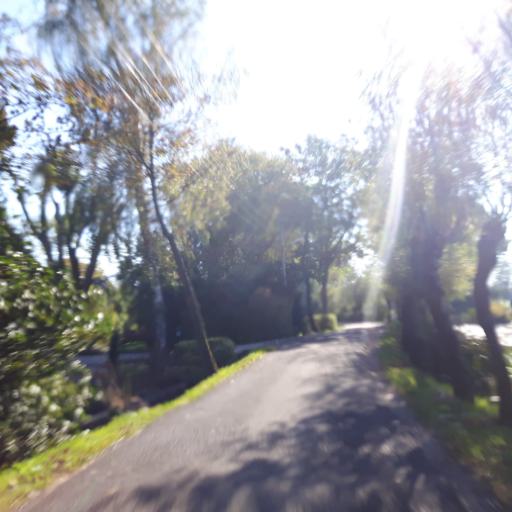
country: NL
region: South Holland
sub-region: Gemeente Vlist
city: Vlist
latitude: 51.9703
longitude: 4.8296
